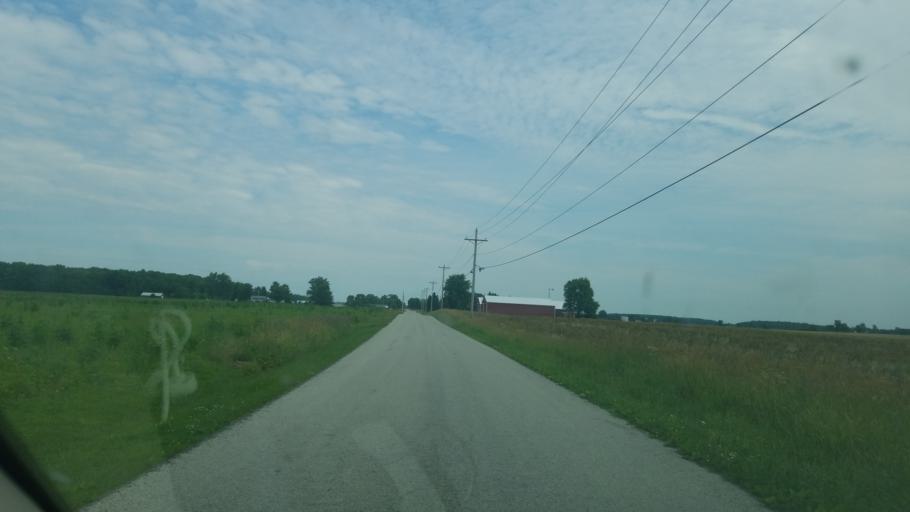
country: US
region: Ohio
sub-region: Seneca County
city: Fostoria
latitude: 41.0575
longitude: -83.4633
